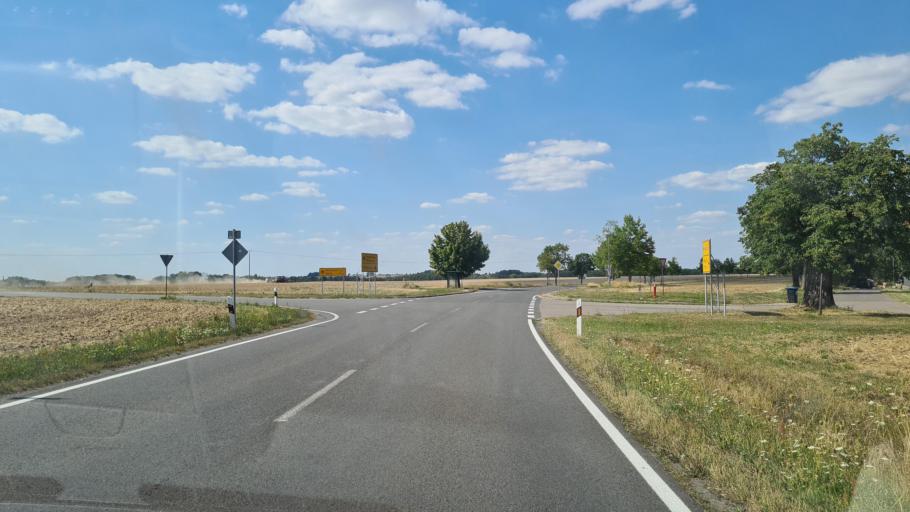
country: DE
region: Saxony
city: Machern
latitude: 51.4113
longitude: 12.6365
